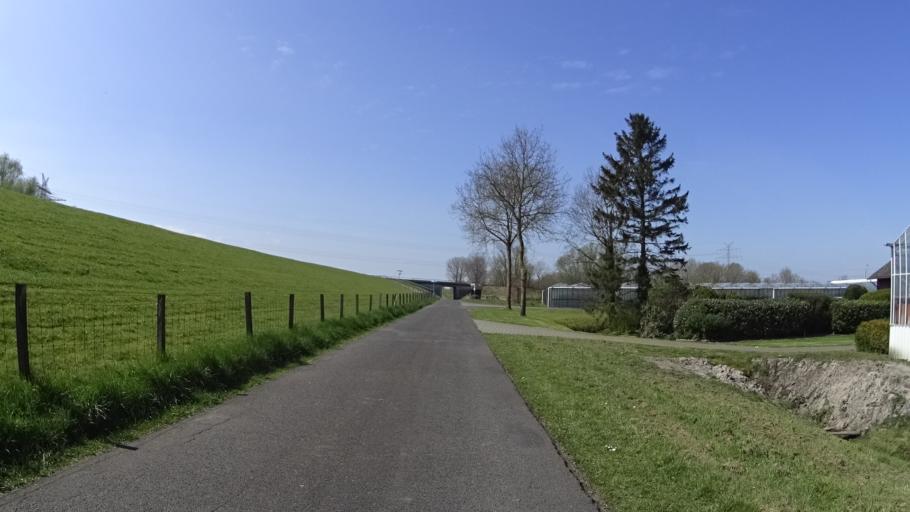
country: DE
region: Lower Saxony
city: Weener
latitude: 53.1054
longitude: 7.3535
